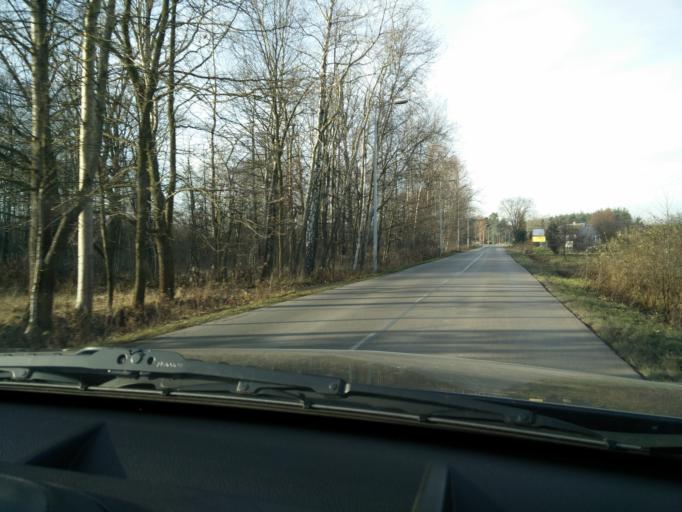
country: PL
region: Masovian Voivodeship
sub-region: Powiat wolominski
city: Duczki
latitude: 52.3105
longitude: 21.3042
